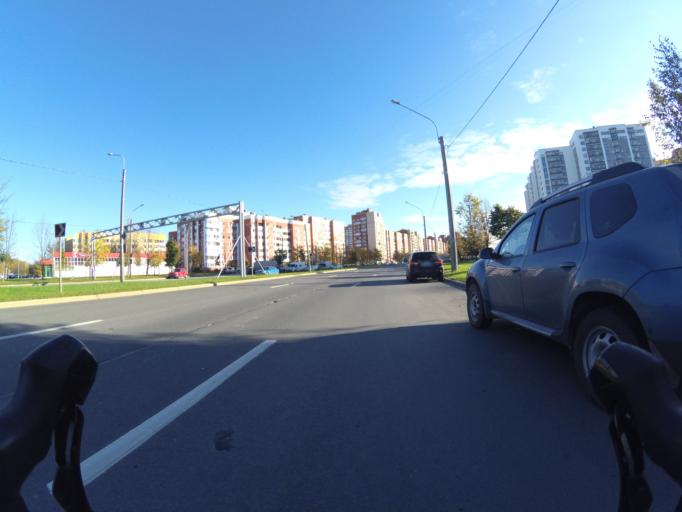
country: RU
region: Leningrad
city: Untolovo
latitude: 60.0085
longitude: 30.2007
